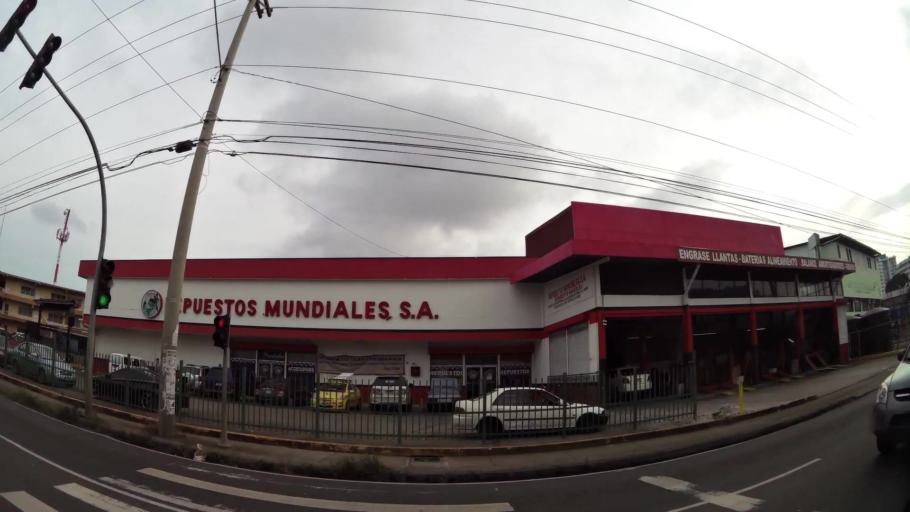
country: PA
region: Panama
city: Panama
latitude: 9.0045
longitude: -79.5142
